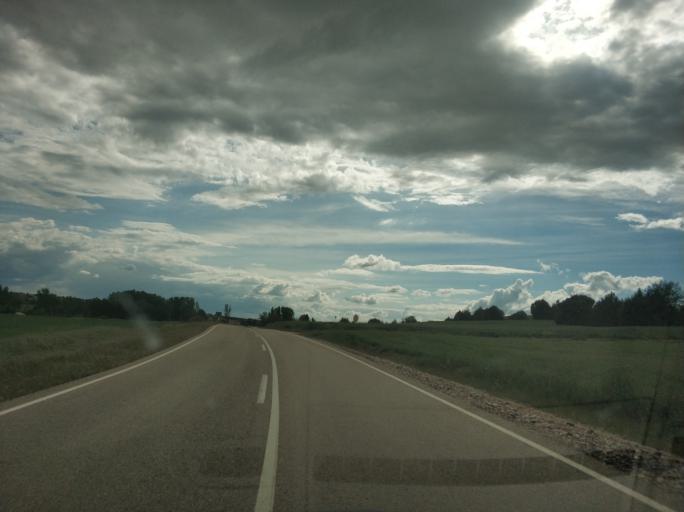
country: ES
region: Castille and Leon
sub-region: Provincia de Burgos
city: Brazacorta
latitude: 41.7210
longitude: -3.3365
